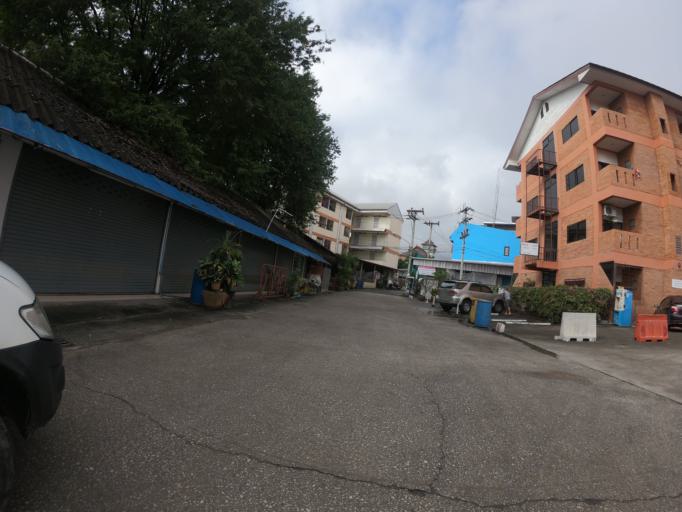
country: TH
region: Chiang Mai
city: Chiang Mai
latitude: 18.8039
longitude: 98.9762
